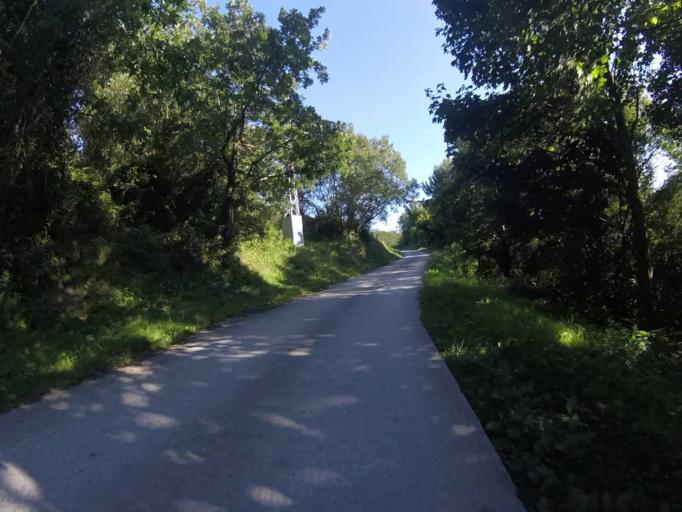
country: ES
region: Basque Country
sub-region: Provincia de Guipuzcoa
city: Fuenterrabia
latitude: 43.3839
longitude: -1.7997
